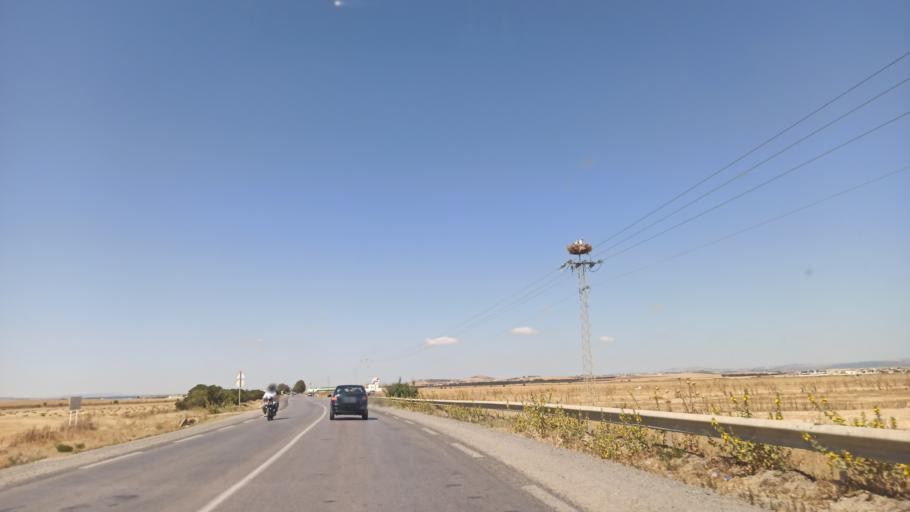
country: TN
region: Tunis
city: Oued Lill
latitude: 36.7464
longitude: 9.9662
